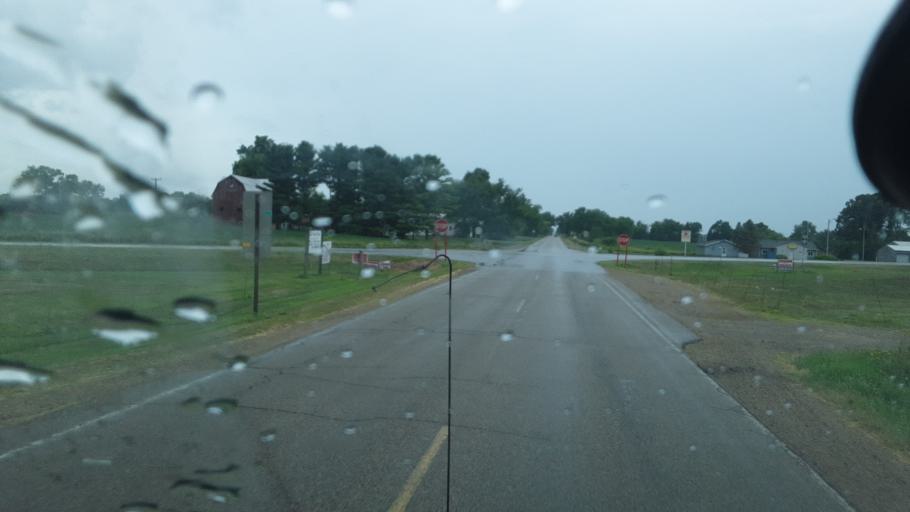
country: US
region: Michigan
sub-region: Hillsdale County
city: Reading
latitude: 41.7081
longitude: -84.7497
